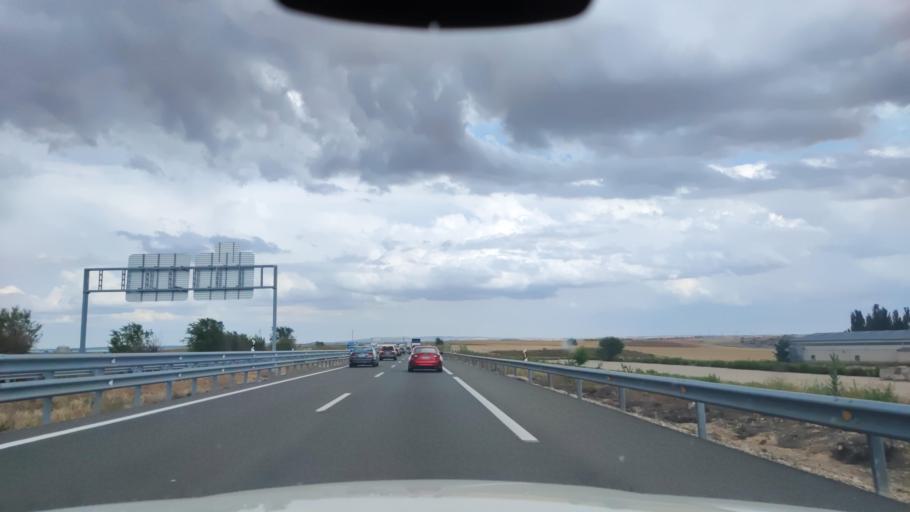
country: ES
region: Castille-La Mancha
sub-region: Provincia de Cuenca
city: Tarancon
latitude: 39.9942
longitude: -3.0057
